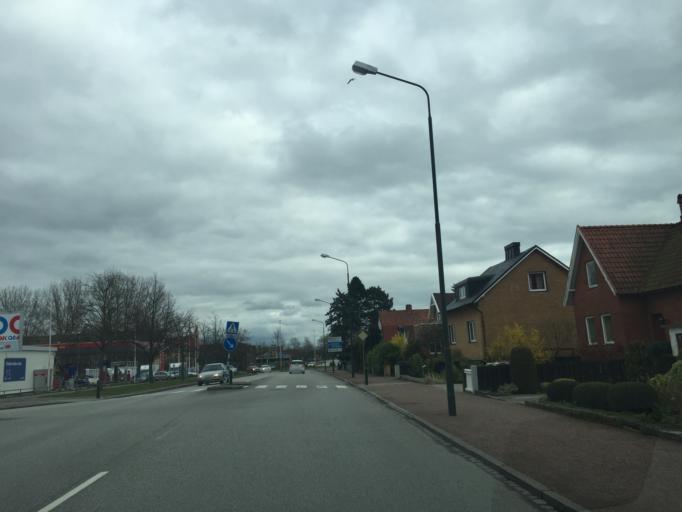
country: SE
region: Skane
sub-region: Malmo
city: Malmoe
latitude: 55.5802
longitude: 12.9739
